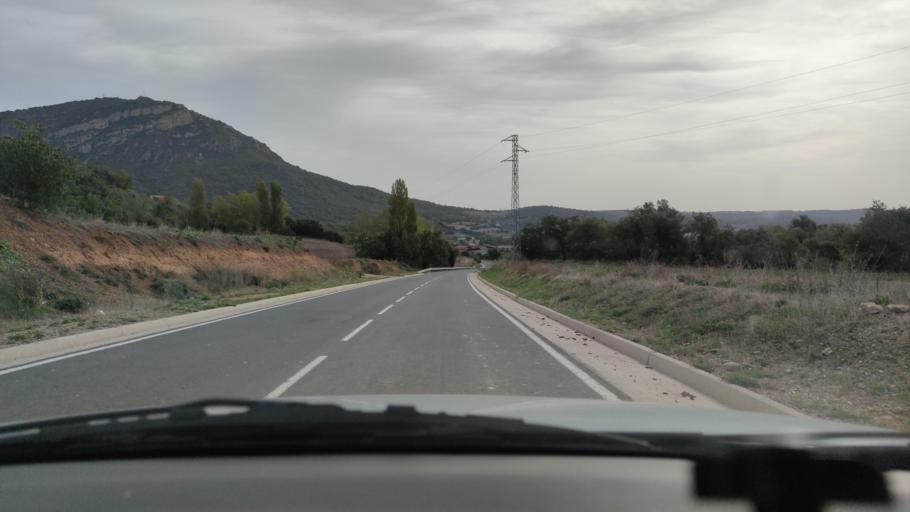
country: ES
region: Catalonia
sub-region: Provincia de Lleida
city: Artesa de Segre
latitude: 41.9939
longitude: 1.0118
